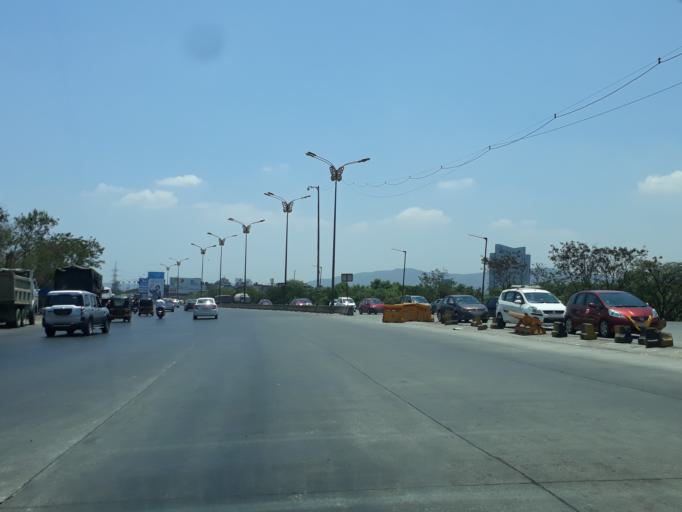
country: IN
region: Maharashtra
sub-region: Thane
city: Navi Mumbai
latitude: 19.0649
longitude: 72.9814
